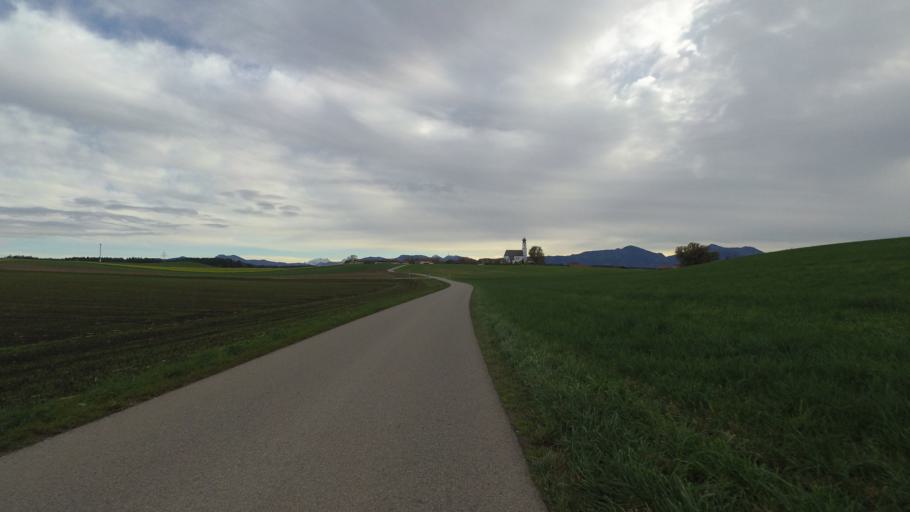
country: DE
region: Bavaria
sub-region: Upper Bavaria
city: Nussdorf
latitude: 47.9114
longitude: 12.5948
